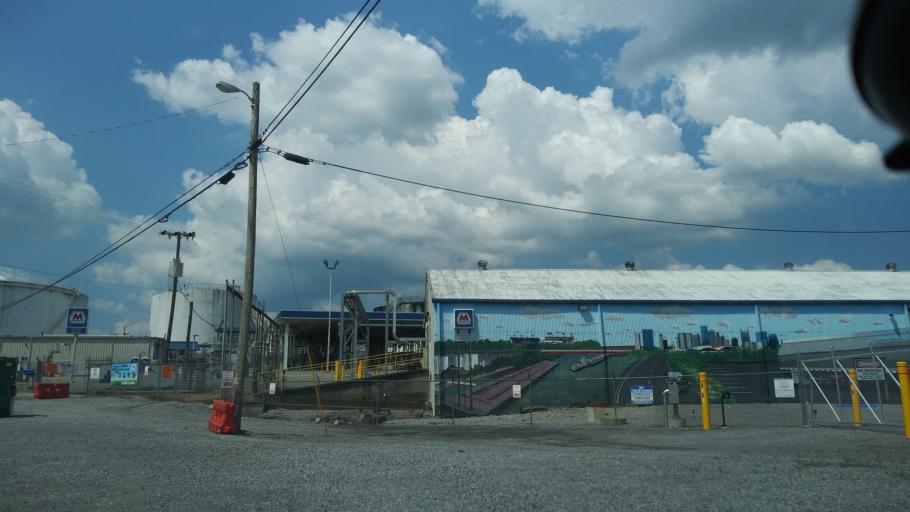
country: US
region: Tennessee
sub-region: Davidson County
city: Nashville
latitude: 36.1640
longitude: -86.8492
